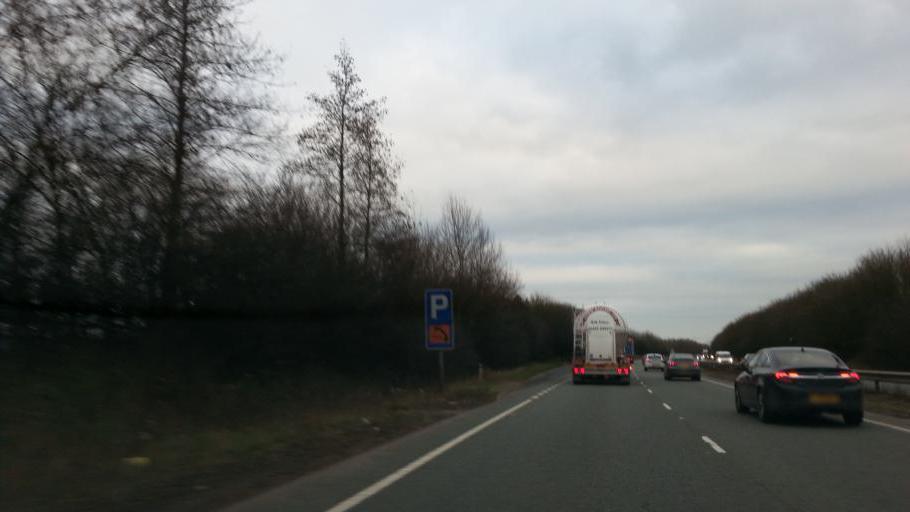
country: GB
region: England
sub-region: Leicestershire
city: Market Harborough
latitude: 52.4070
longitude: -0.9601
